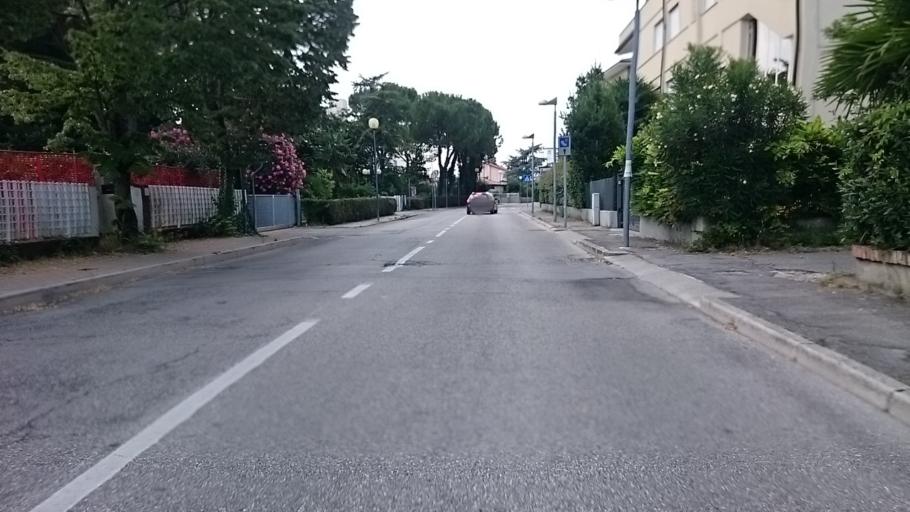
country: IT
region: Veneto
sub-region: Provincia di Padova
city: Abano Terme
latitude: 45.3454
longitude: 11.7845
